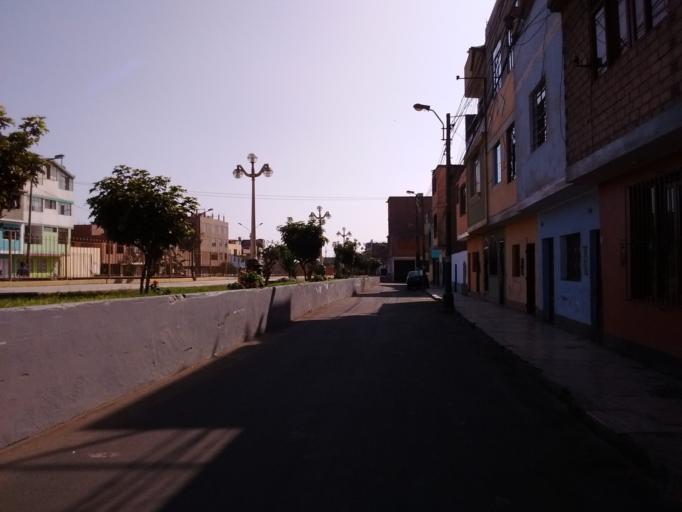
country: PE
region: Callao
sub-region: Callao
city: Callao
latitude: -12.0391
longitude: -77.0830
